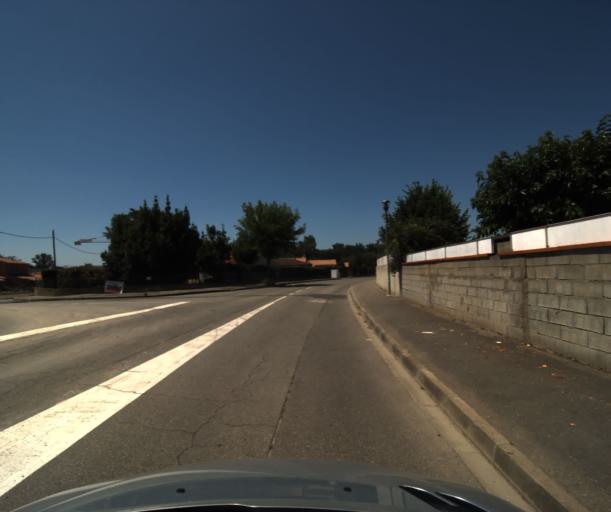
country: FR
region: Midi-Pyrenees
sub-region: Departement de la Haute-Garonne
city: Roquettes
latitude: 43.4943
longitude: 1.3683
